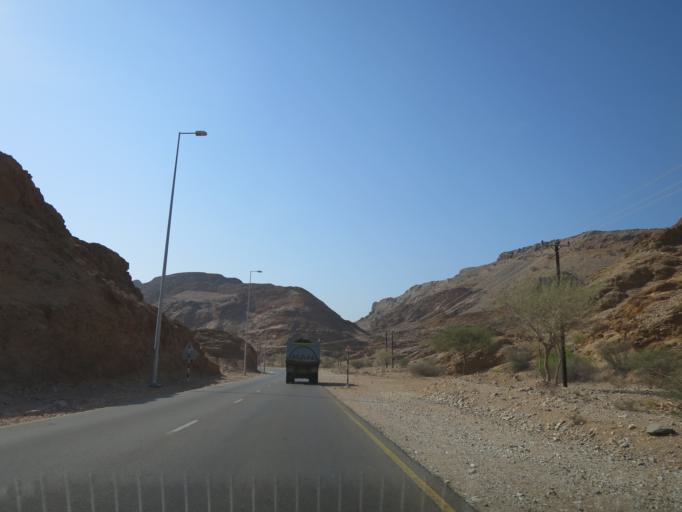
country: OM
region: Muhafazat Masqat
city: Muscat
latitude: 23.5172
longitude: 58.7101
